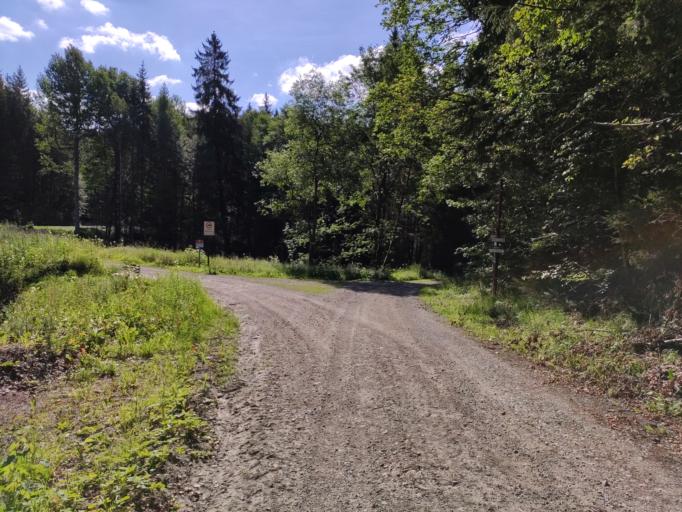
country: DE
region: Bavaria
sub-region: Upper Franconia
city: Nordhalben
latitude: 50.4066
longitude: 11.5457
